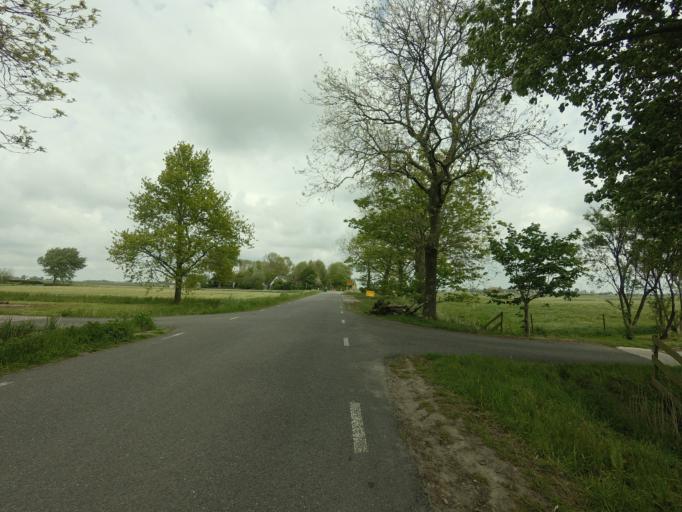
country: NL
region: Friesland
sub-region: Sudwest Fryslan
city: Bolsward
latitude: 53.1047
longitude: 5.5418
